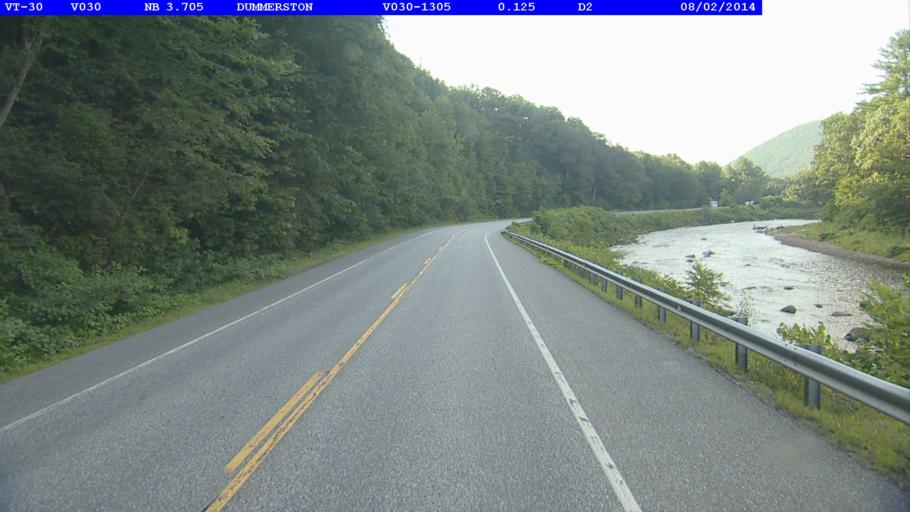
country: US
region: Vermont
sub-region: Windham County
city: West Brattleboro
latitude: 42.8991
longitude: -72.6001
